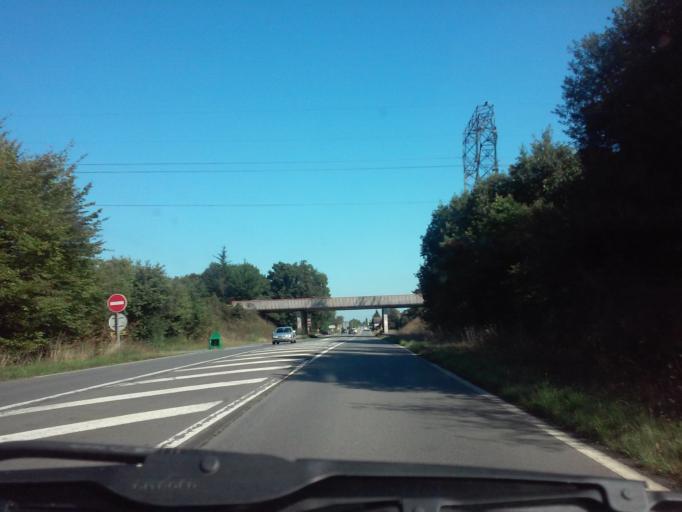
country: FR
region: Brittany
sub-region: Departement d'Ille-et-Vilaine
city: Betton
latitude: 48.1588
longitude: -1.6493
